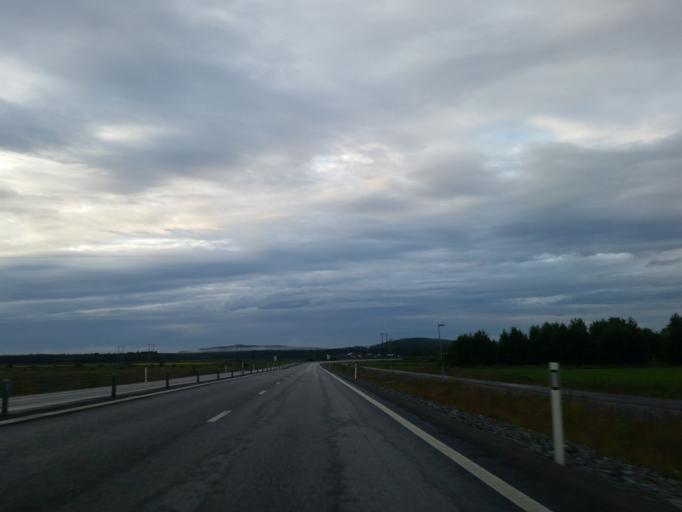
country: SE
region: Vaesterbotten
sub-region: Umea Kommun
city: Roback
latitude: 63.8471
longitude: 20.1907
